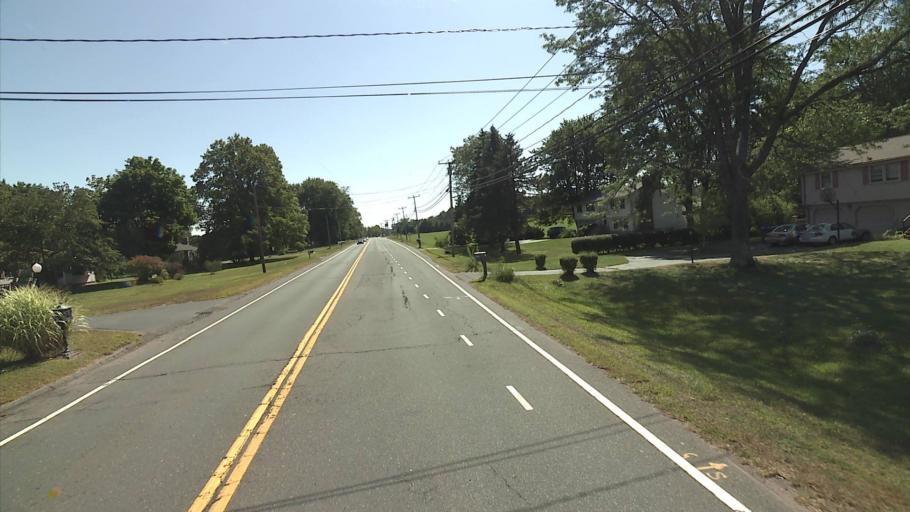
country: US
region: Connecticut
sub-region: Hartford County
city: Thompsonville
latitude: 41.9841
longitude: -72.6134
